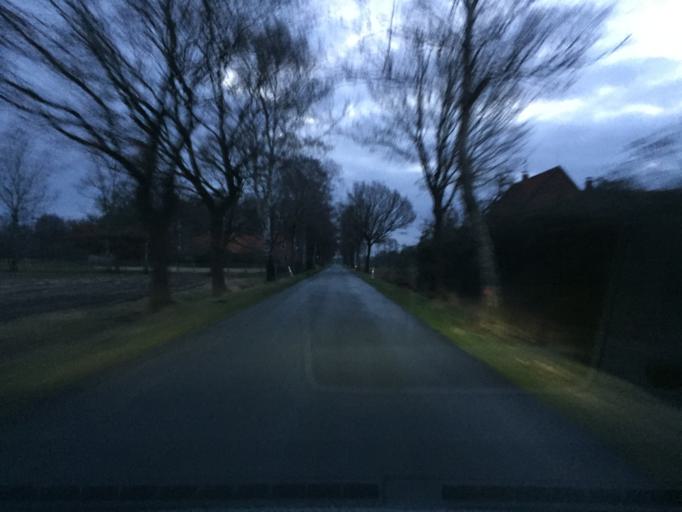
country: DE
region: Lower Saxony
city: Kirchdorf
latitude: 52.6374
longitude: 8.8424
